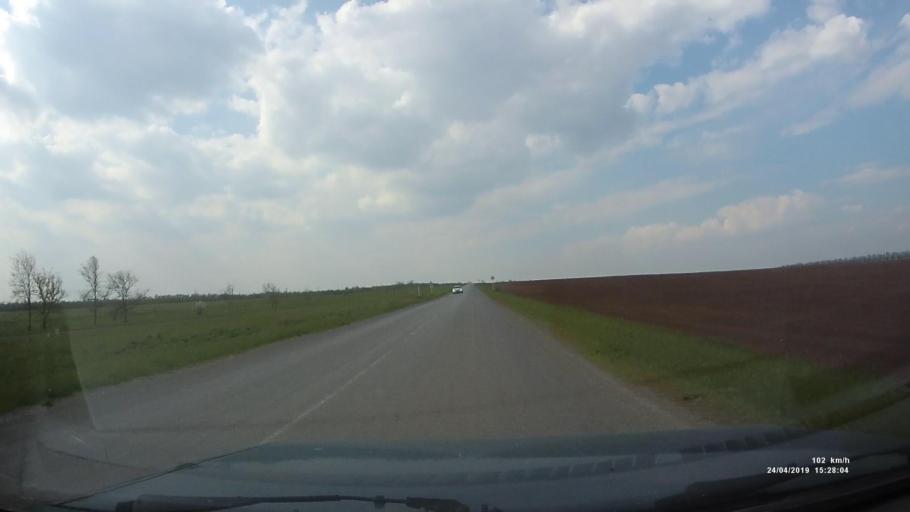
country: RU
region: Rostov
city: Remontnoye
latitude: 46.5738
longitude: 43.0211
